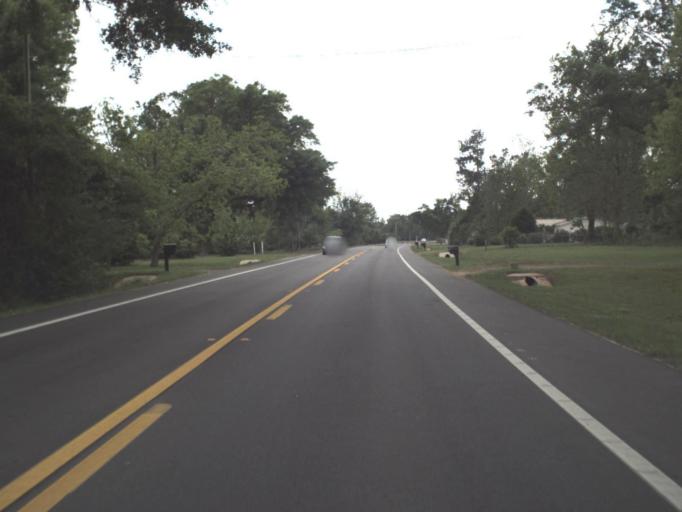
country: US
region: Florida
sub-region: Escambia County
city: Century
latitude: 30.9245
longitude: -87.1600
